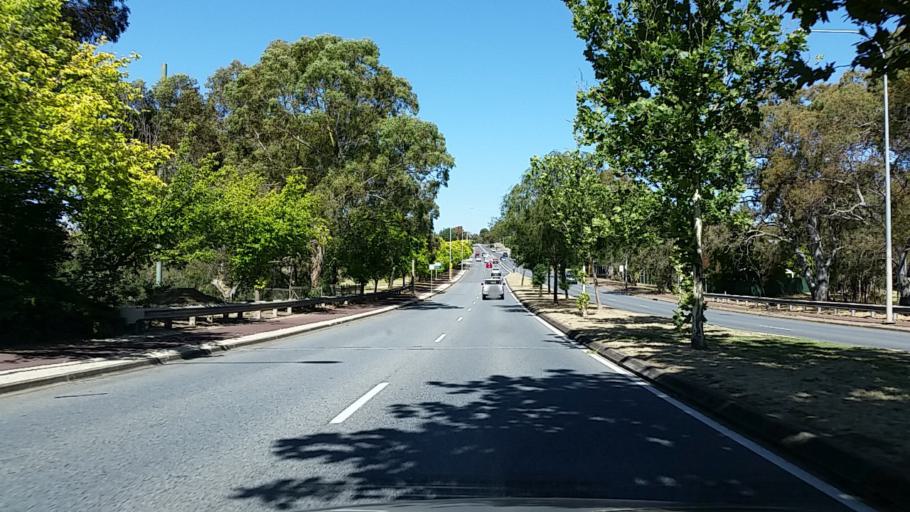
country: AU
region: South Australia
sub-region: Tea Tree Gully
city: Golden Grove
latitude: -34.7955
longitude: 138.7056
